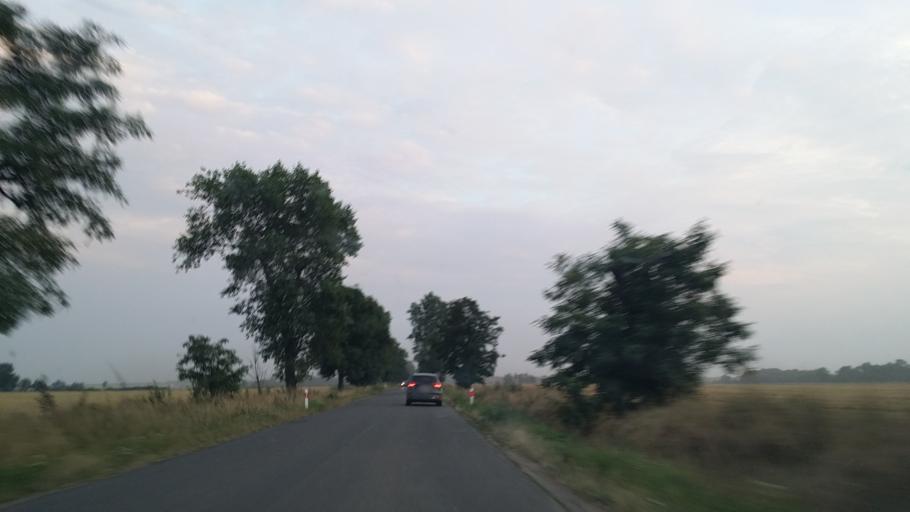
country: PL
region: Lower Silesian Voivodeship
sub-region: Powiat legnicki
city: Prochowice
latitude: 51.2102
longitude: 16.3487
